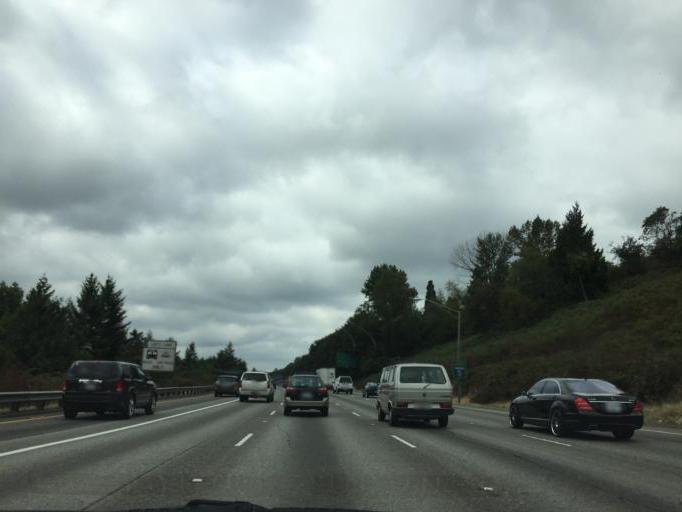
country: US
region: Washington
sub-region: King County
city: SeaTac
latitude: 47.4286
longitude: -122.2758
